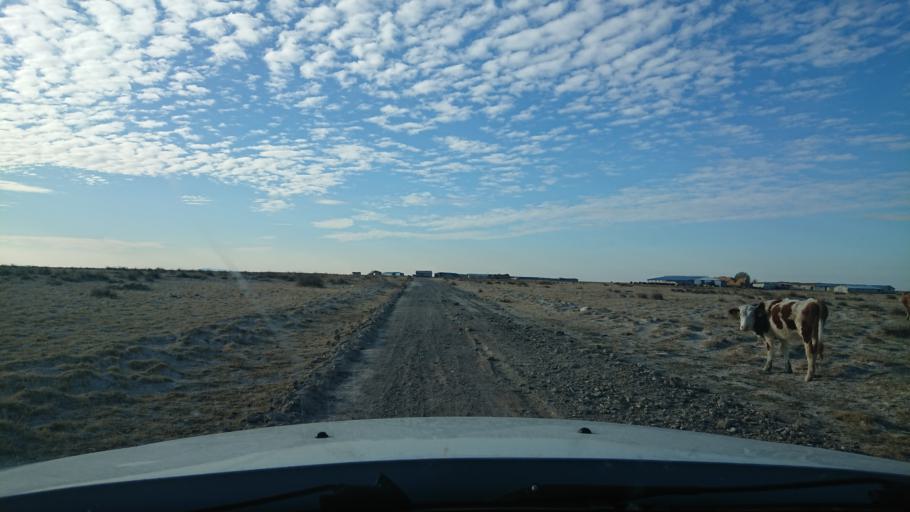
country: TR
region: Aksaray
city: Eskil
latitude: 38.5663
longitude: 33.2983
